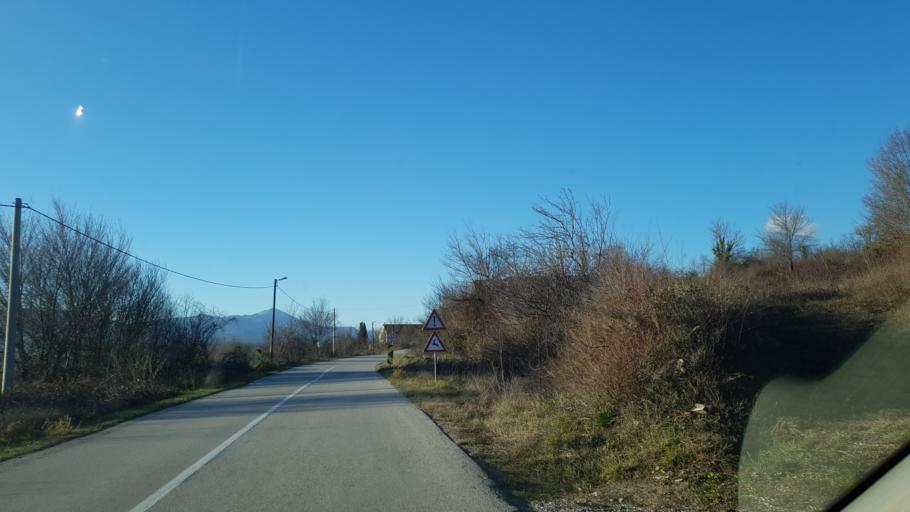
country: HR
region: Splitsko-Dalmatinska
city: Gala
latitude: 43.7331
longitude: 16.6883
